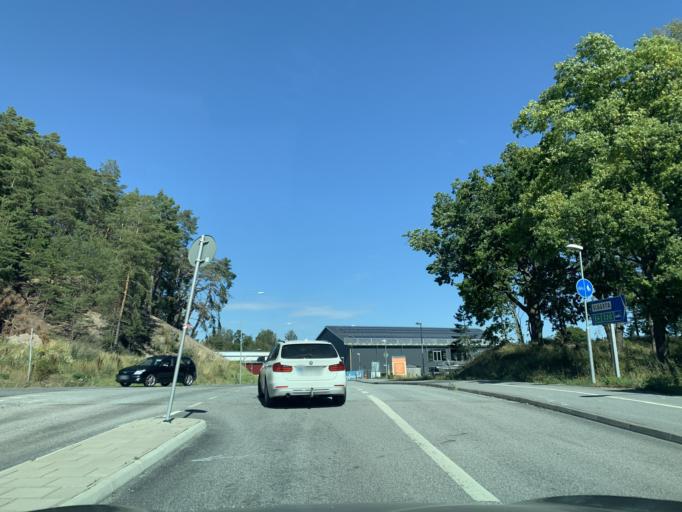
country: SE
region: Stockholm
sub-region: Botkyrka Kommun
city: Fittja
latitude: 59.2733
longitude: 17.8446
